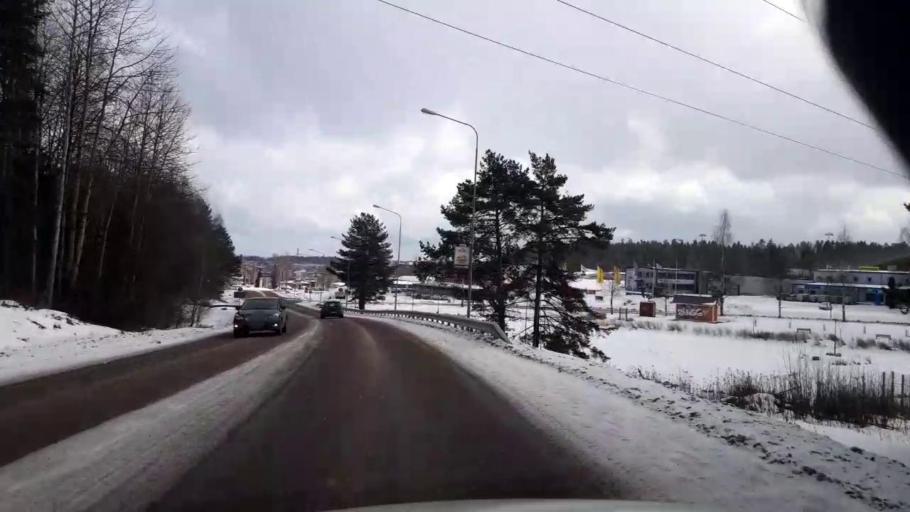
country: SE
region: Gaevleborg
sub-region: Hudiksvalls Kommun
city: Hudiksvall
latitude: 61.7368
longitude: 17.0903
